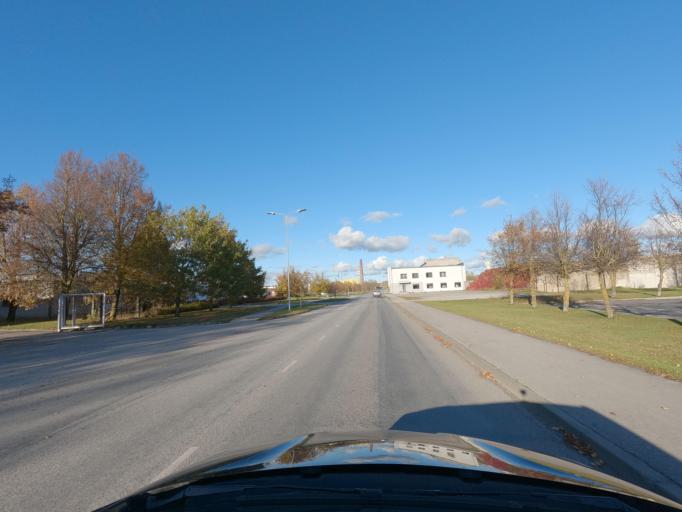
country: EE
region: Saare
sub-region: Kuressaare linn
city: Kuressaare
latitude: 58.2650
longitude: 22.4871
